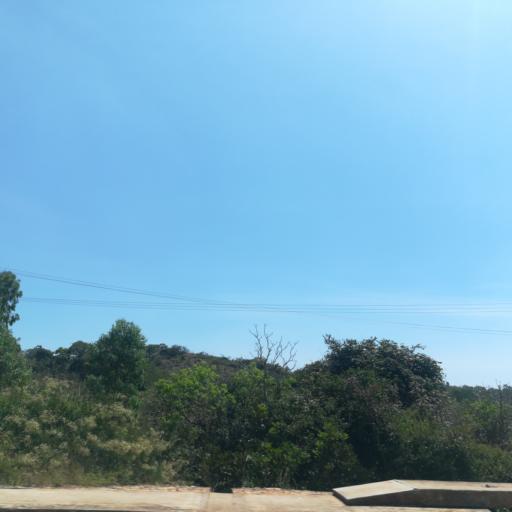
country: NG
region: Plateau
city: Bukuru
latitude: 9.8117
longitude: 8.8728
